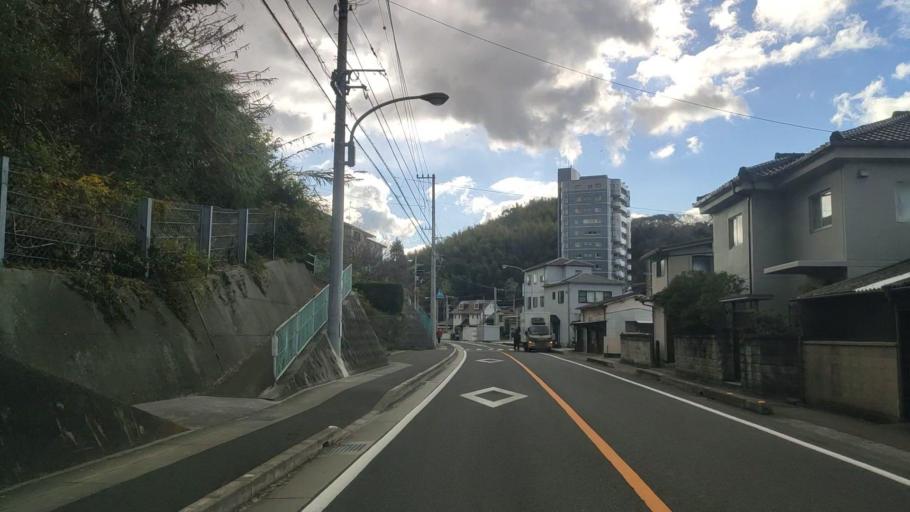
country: JP
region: Ehime
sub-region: Shikoku-chuo Shi
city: Matsuyama
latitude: 33.8711
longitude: 132.7102
